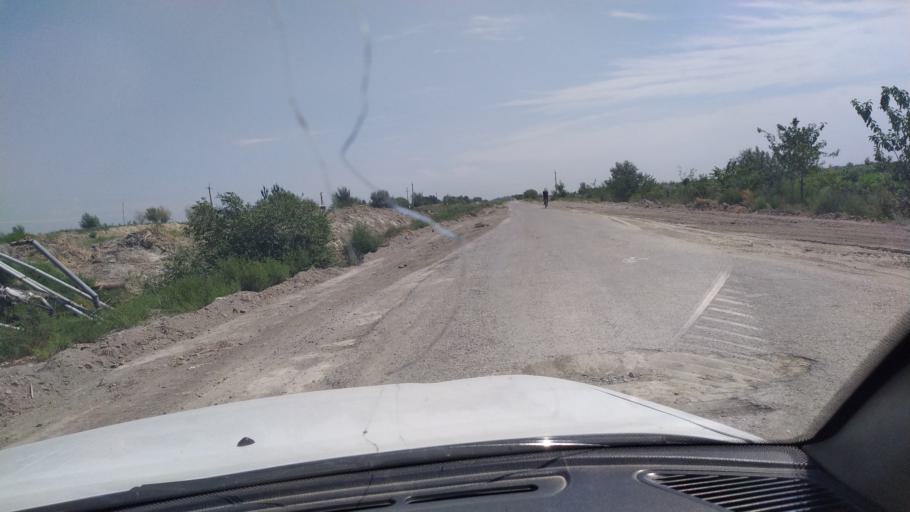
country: UZ
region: Namangan
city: Toshbuloq
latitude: 40.7923
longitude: 71.5728
